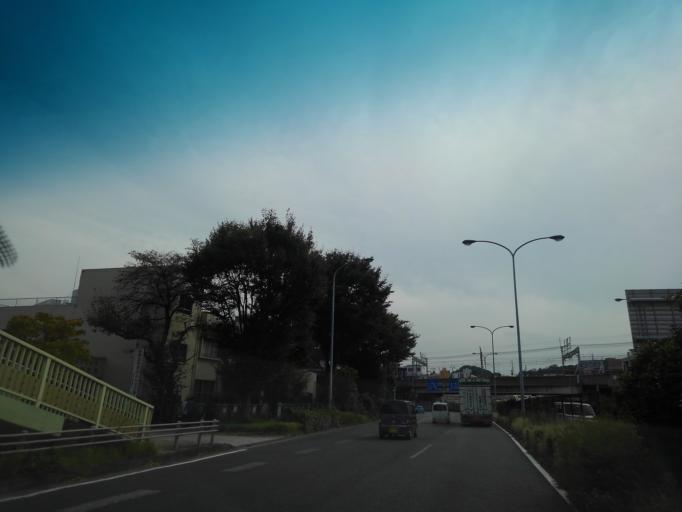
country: JP
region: Tokyo
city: Hachioji
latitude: 35.6463
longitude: 139.3527
